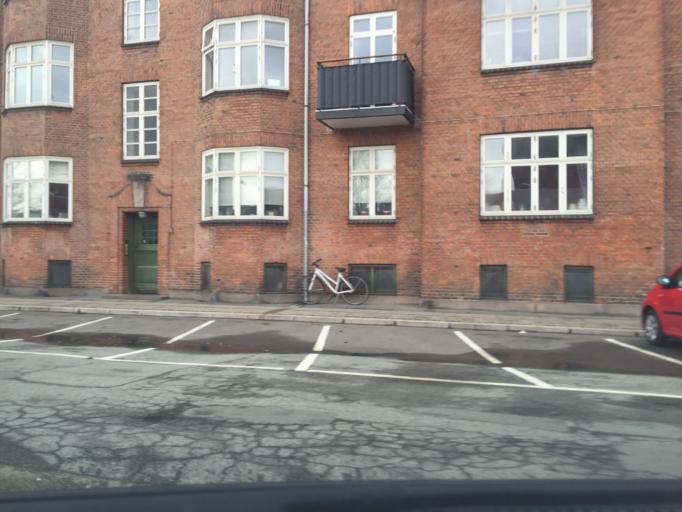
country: DK
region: Capital Region
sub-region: Kobenhavn
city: Christianshavn
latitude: 55.6607
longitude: 12.5996
